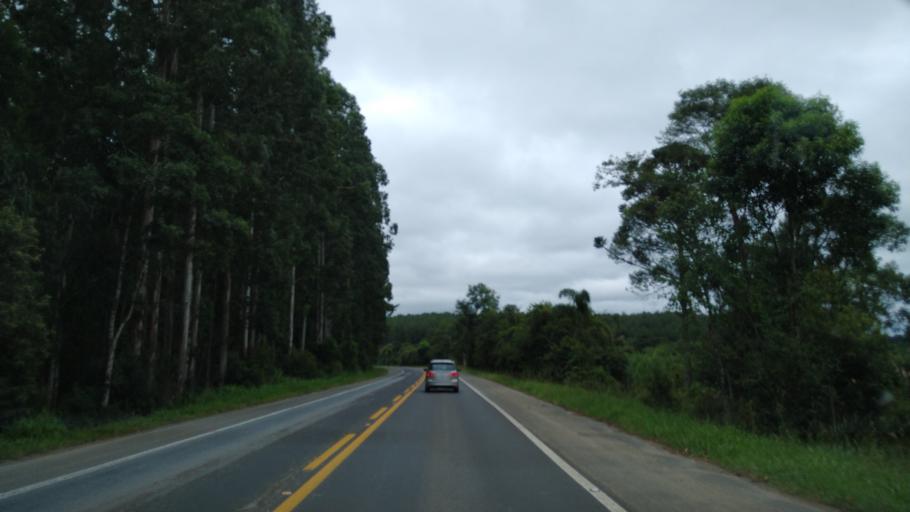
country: BR
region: Santa Catarina
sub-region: Tres Barras
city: Tres Barras
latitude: -26.1642
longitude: -50.1403
